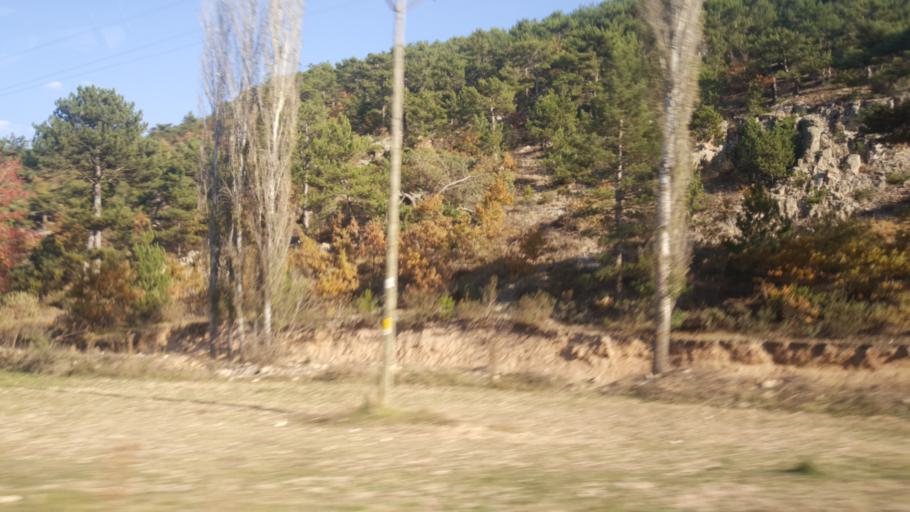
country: TR
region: Eskisehir
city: Kirka
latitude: 39.1370
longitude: 30.5949
